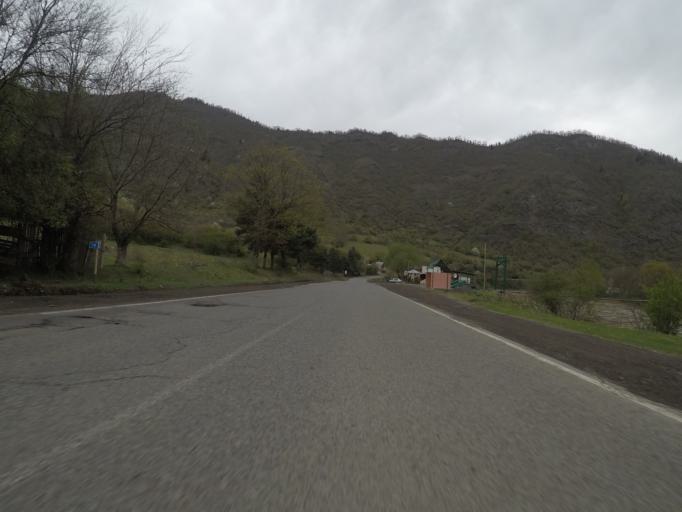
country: GE
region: Samtskhe-Javakheti
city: Borjomi
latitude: 41.8937
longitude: 43.4379
